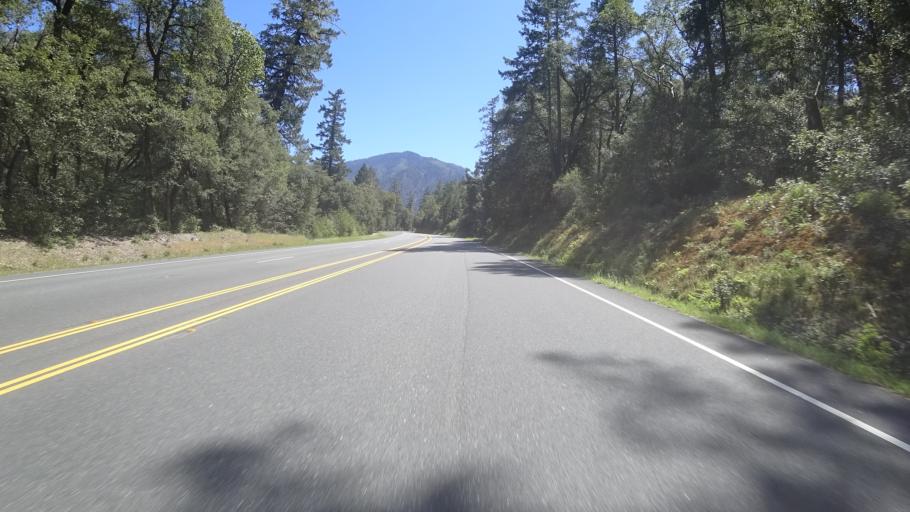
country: US
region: California
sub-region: Humboldt County
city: Willow Creek
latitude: 40.8592
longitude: -123.4979
